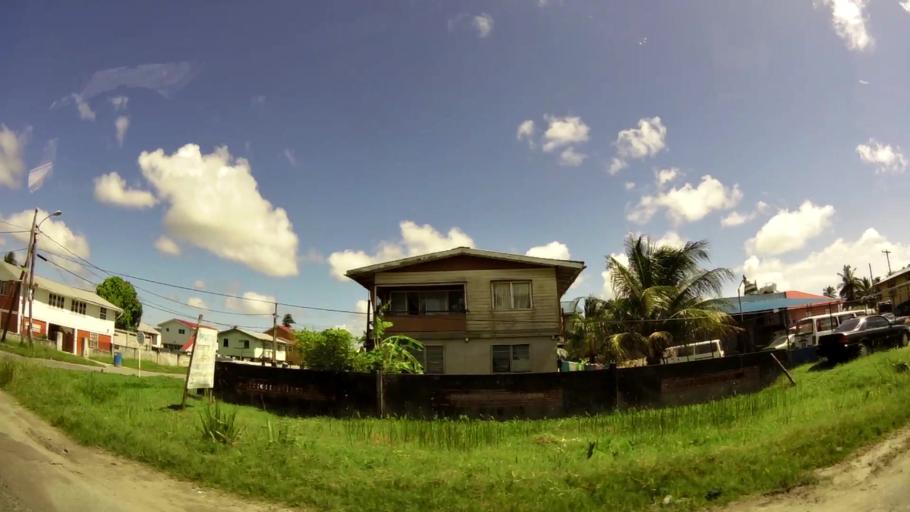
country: GY
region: Demerara-Mahaica
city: Georgetown
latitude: 6.7833
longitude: -58.1292
